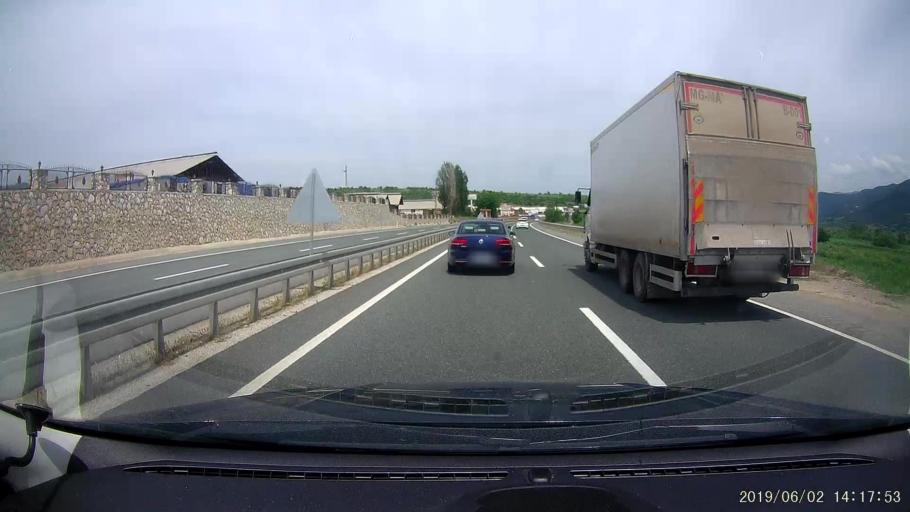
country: TR
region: Kastamonu
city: Tosya
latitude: 40.9567
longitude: 33.9422
